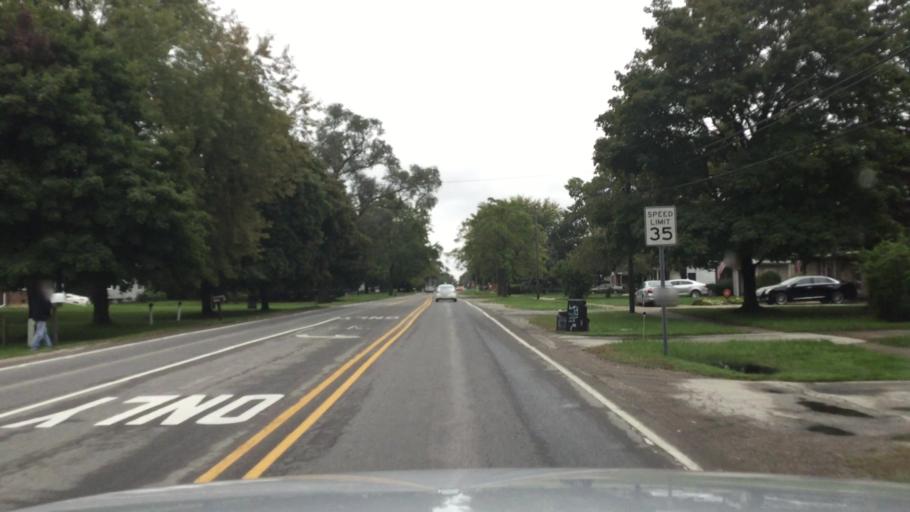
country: US
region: Michigan
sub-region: Saginaw County
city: Shields
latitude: 43.4437
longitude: -84.0050
